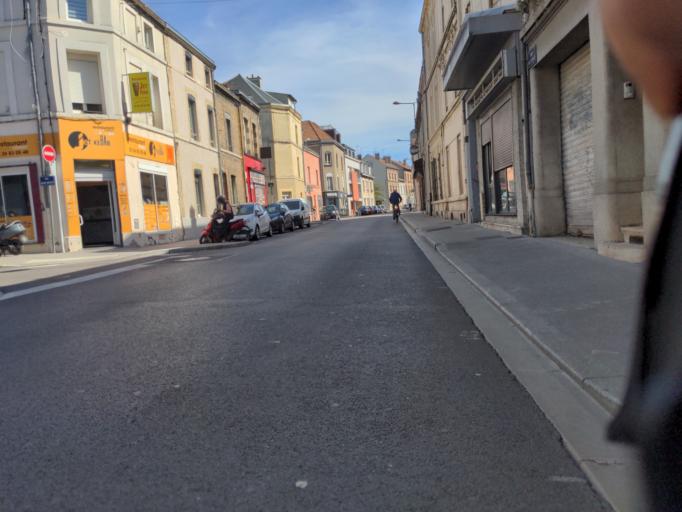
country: FR
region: Champagne-Ardenne
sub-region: Departement de la Marne
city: Reims
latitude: 49.2579
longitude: 4.0536
